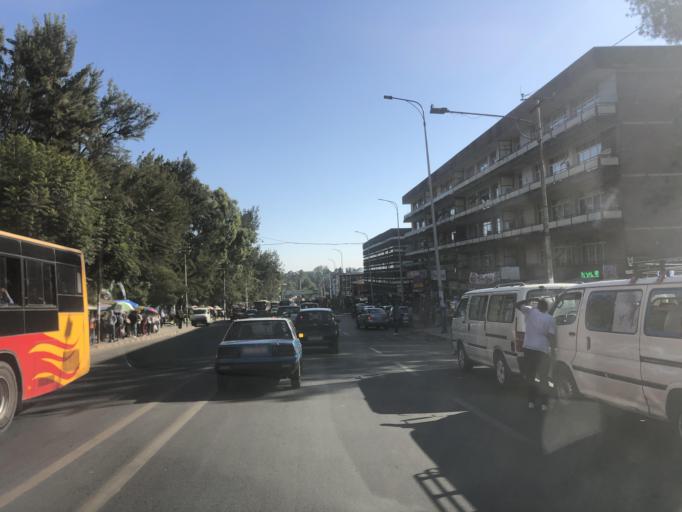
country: ET
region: Adis Abeba
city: Addis Ababa
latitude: 9.0358
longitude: 38.7630
